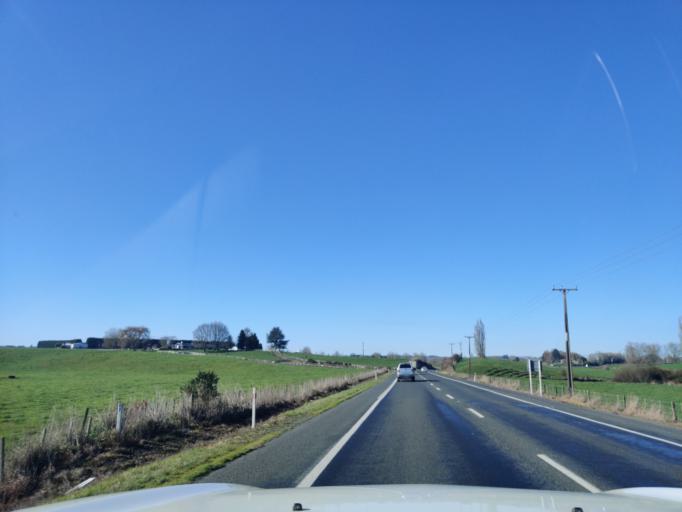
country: NZ
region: Waikato
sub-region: Matamata-Piako District
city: Matamata
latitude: -38.0254
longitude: 175.7872
